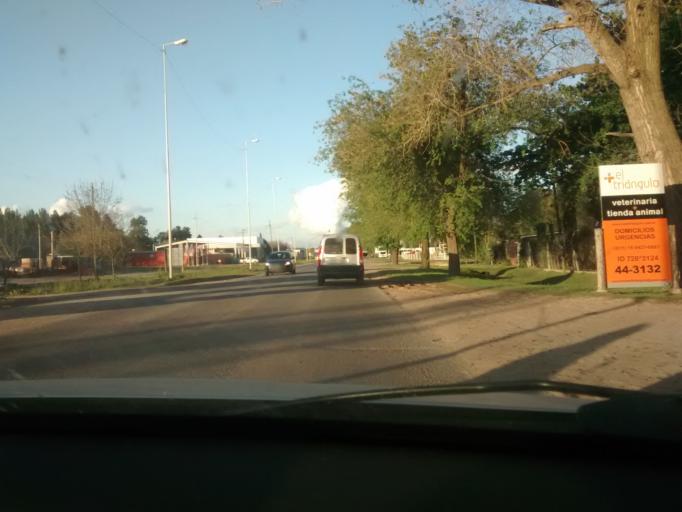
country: AR
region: Buenos Aires
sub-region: Partido de Brandsen
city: Brandsen
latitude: -35.1649
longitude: -58.2226
